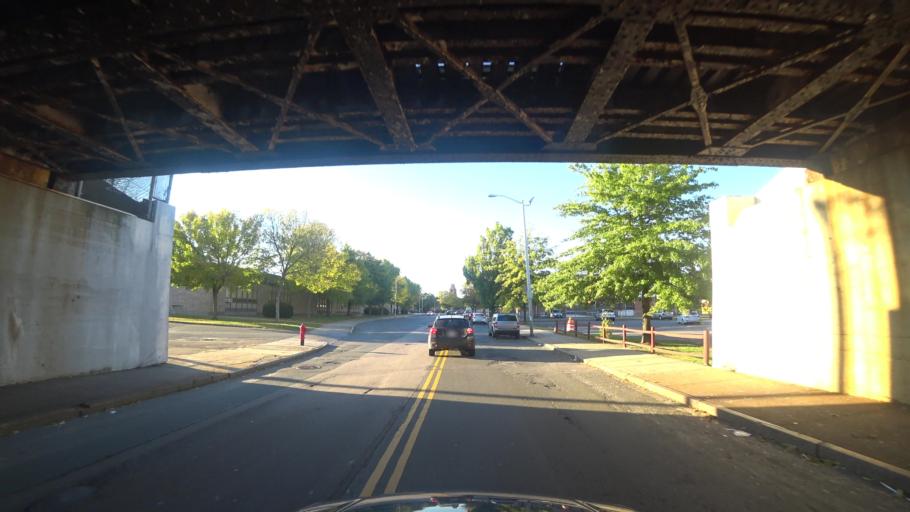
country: US
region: Massachusetts
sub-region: Essex County
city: Lynn
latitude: 42.4595
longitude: -70.9528
